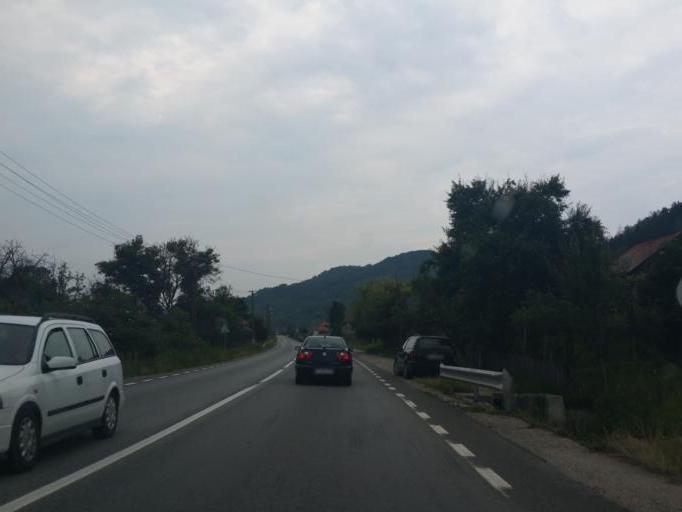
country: RO
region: Salaj
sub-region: Comuna Dragu
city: Dragu
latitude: 46.9517
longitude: 23.3542
